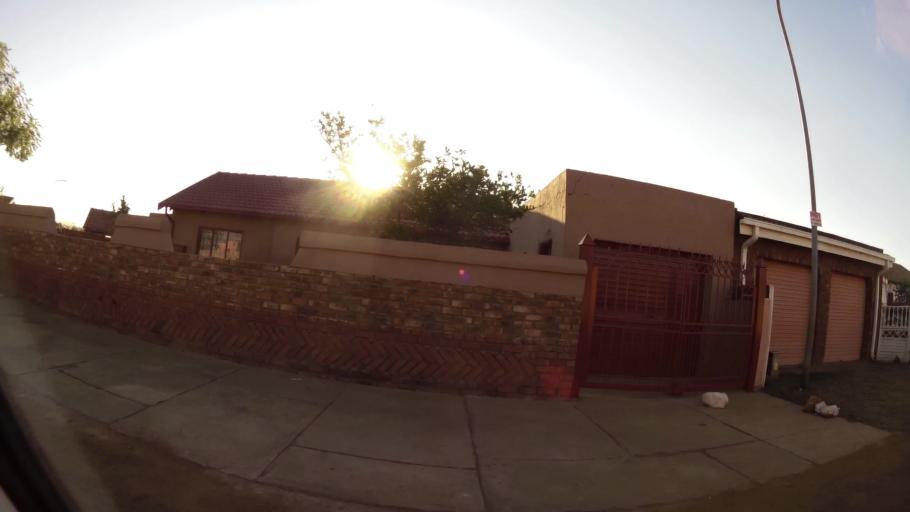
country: ZA
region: Gauteng
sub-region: City of Tshwane Metropolitan Municipality
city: Cullinan
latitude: -25.7289
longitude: 28.3991
